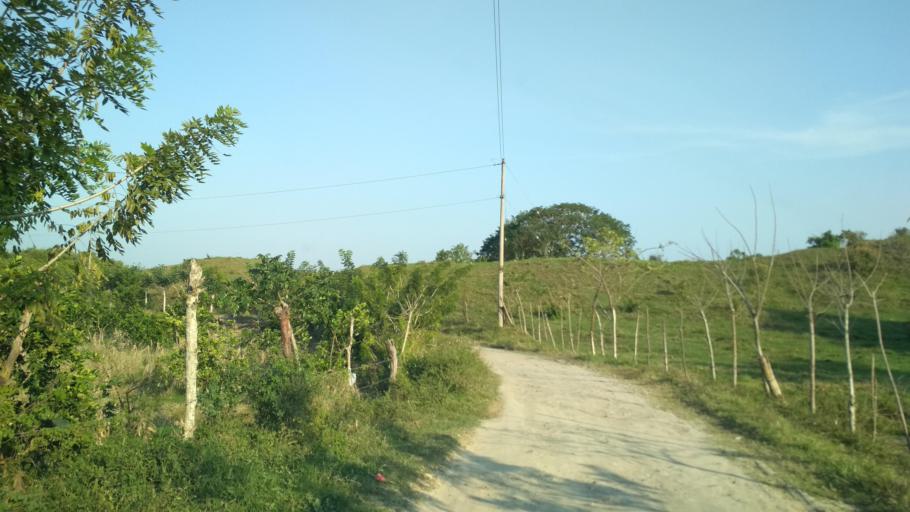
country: MX
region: Puebla
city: San Jose Acateno
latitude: 20.2284
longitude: -97.2575
